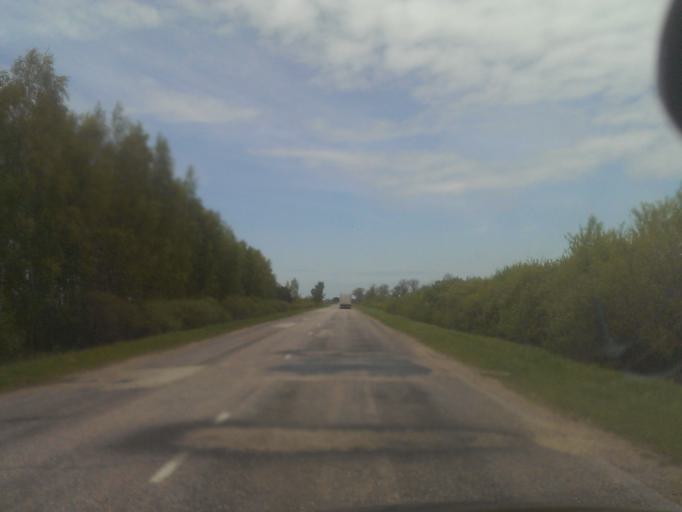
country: LV
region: Ventspils Rajons
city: Piltene
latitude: 57.1873
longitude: 21.6424
